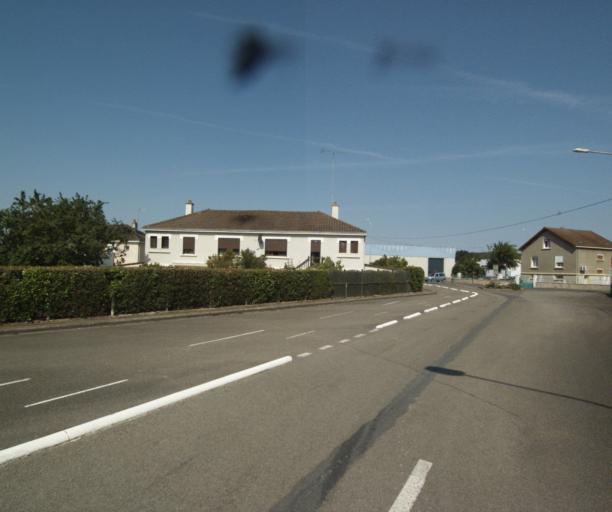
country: FR
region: Bourgogne
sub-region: Departement de Saone-et-Loire
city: Gueugnon
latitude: 46.5964
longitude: 4.0534
